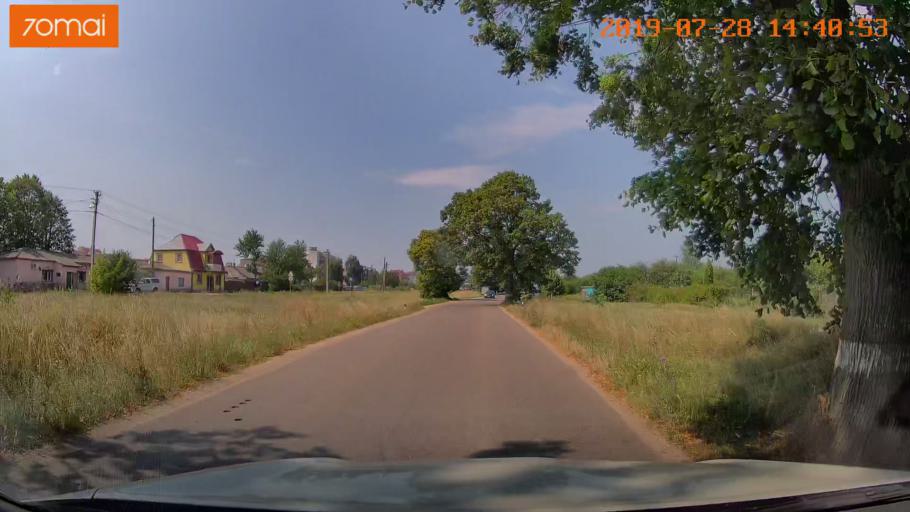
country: RU
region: Kaliningrad
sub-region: Gorod Kaliningrad
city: Yantarnyy
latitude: 54.8539
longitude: 19.9529
